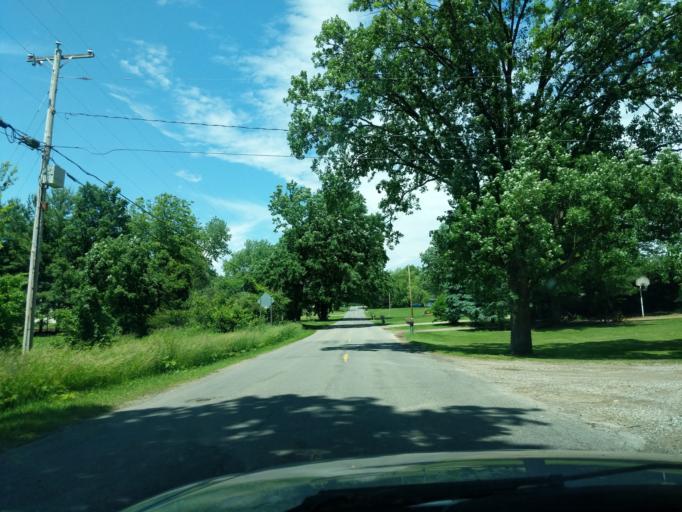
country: US
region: Michigan
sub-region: Jackson County
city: Michigan Center
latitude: 42.1894
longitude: -84.3070
